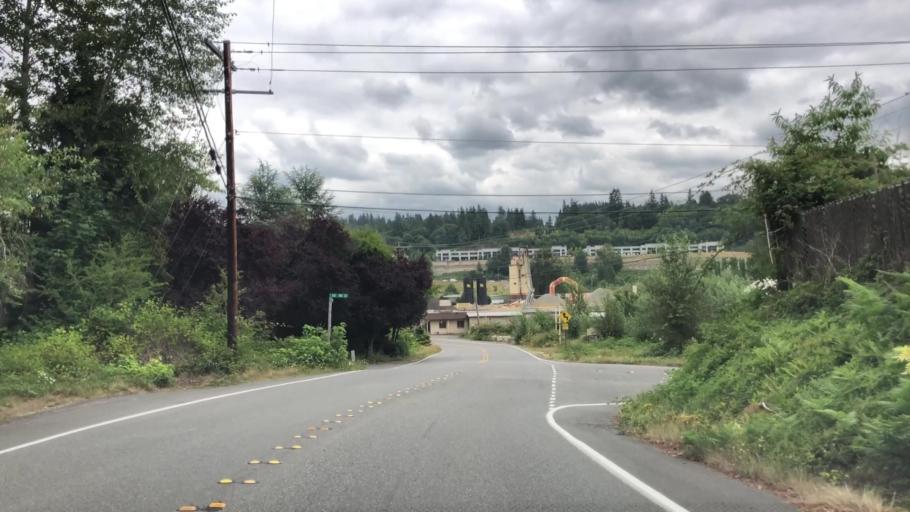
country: US
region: Washington
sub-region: King County
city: Woodinville
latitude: 47.7815
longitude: -122.1555
